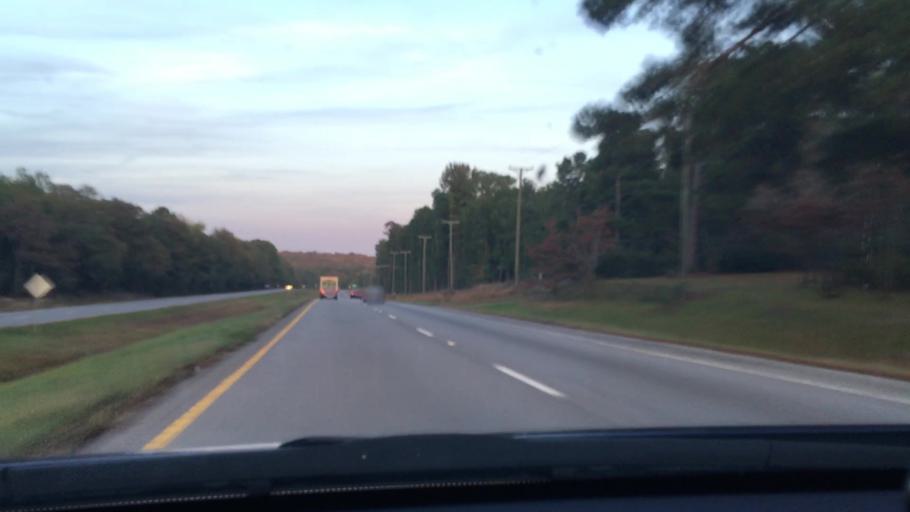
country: US
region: South Carolina
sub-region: Richland County
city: Gadsden
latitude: 33.9431
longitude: -80.7689
